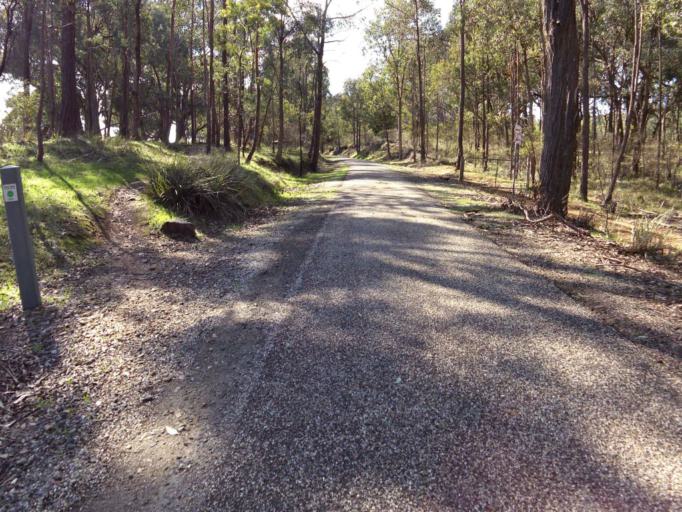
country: AU
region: Victoria
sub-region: Wangaratta
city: Wangaratta
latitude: -36.4031
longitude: 146.6402
